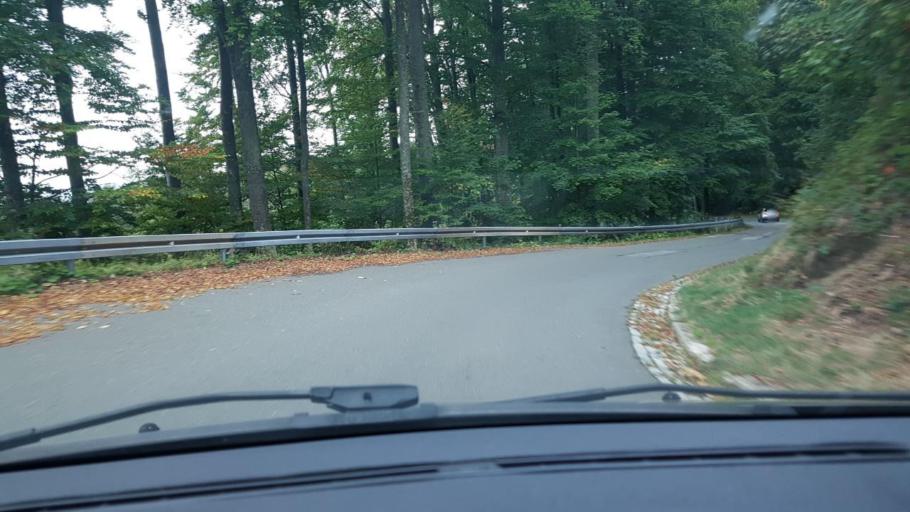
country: HR
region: Grad Zagreb
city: Kasina
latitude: 45.8880
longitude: 15.9367
